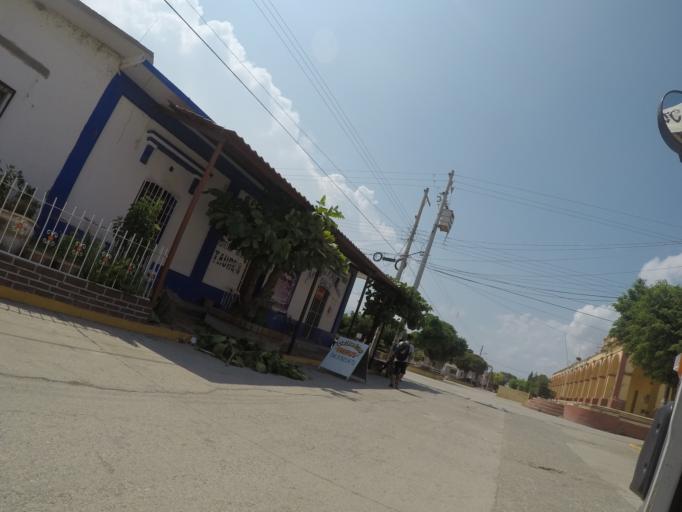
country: MX
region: Oaxaca
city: Union Hidalgo
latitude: 16.4723
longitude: -94.8291
